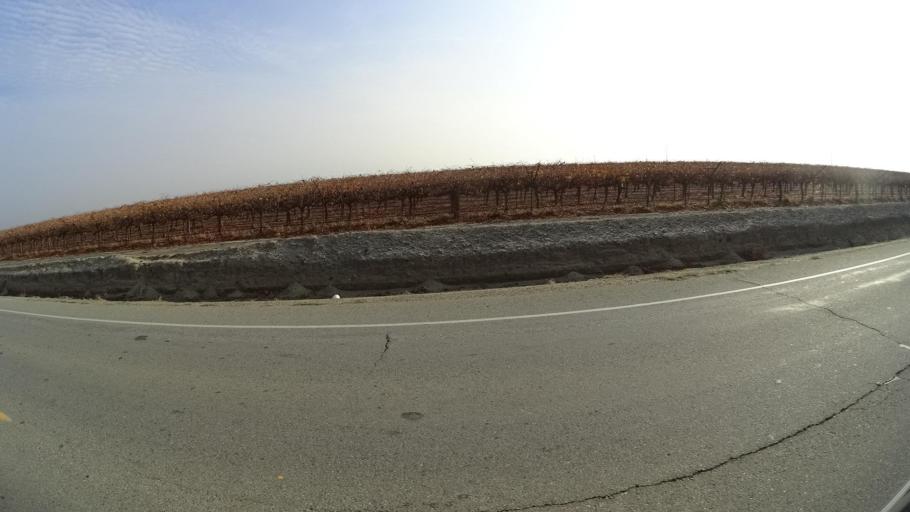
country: US
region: California
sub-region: Kern County
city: Arvin
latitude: 35.0756
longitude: -118.9174
